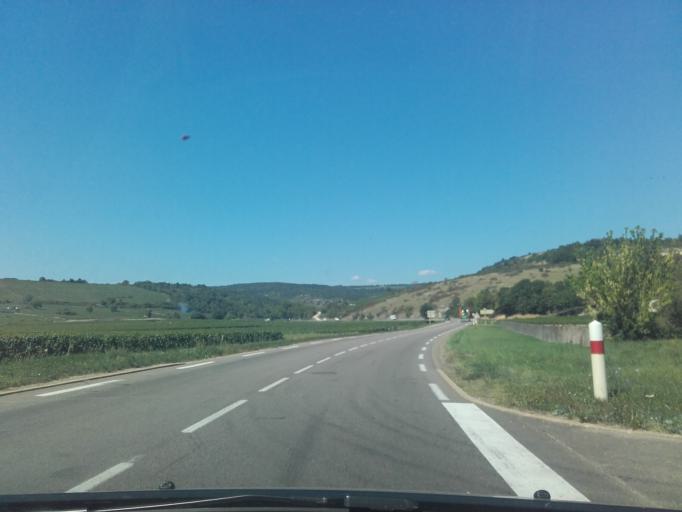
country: FR
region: Bourgogne
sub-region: Departement de la Cote-d'Or
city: Corpeau
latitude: 46.9402
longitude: 4.7357
